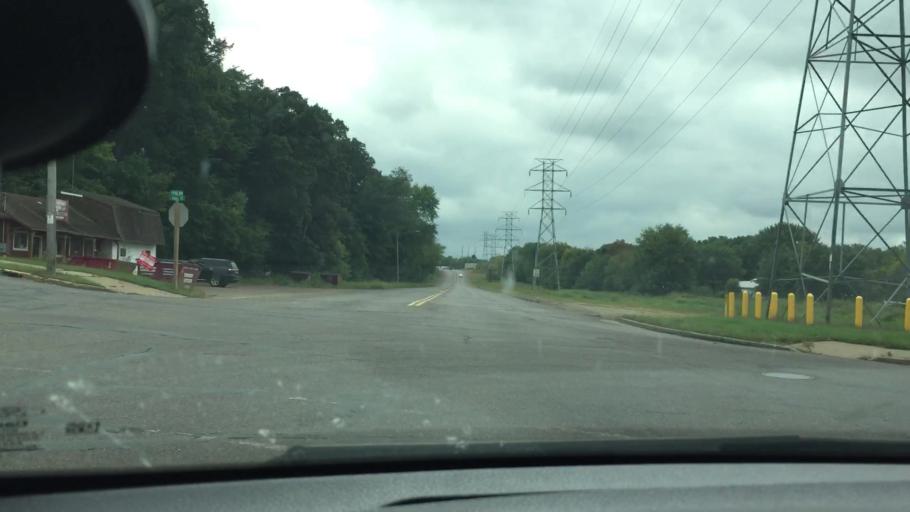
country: US
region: Wisconsin
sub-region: Chippewa County
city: Chippewa Falls
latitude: 44.9242
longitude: -91.3906
